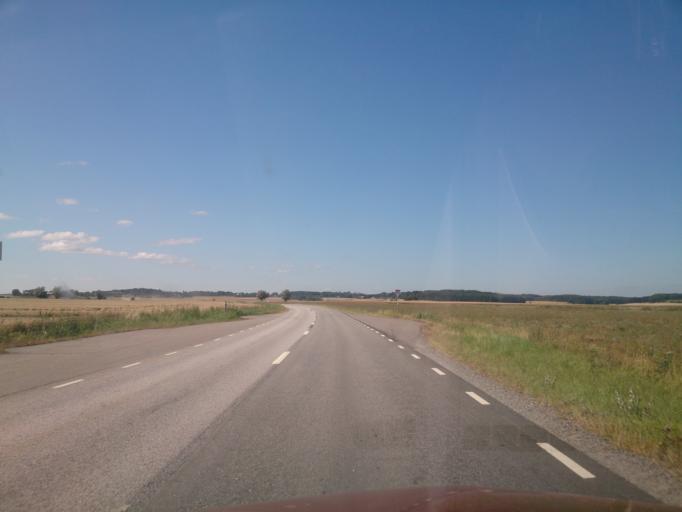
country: SE
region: OEstergoetland
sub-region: Norrkopings Kommun
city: Krokek
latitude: 58.5794
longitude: 16.3629
